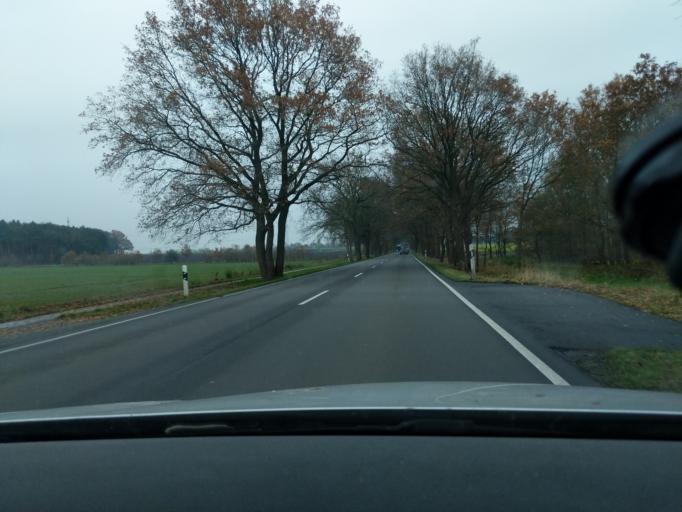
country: DE
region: Lower Saxony
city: Gyhum
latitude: 53.2296
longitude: 9.2888
